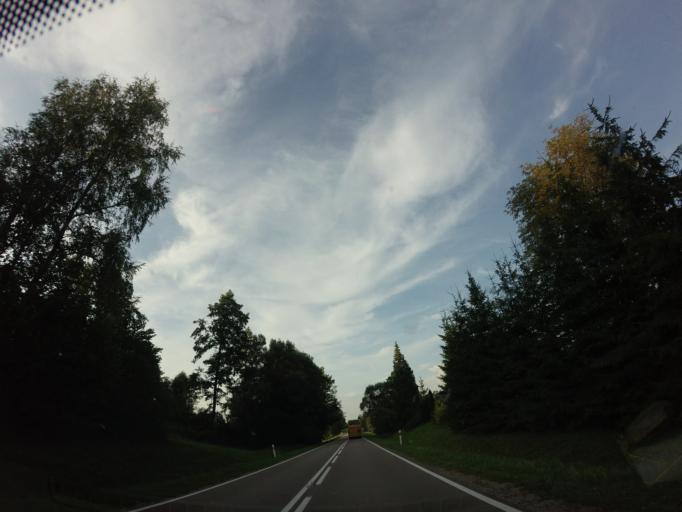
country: PL
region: Podlasie
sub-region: Powiat sejnenski
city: Sejny
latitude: 54.0669
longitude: 23.3614
